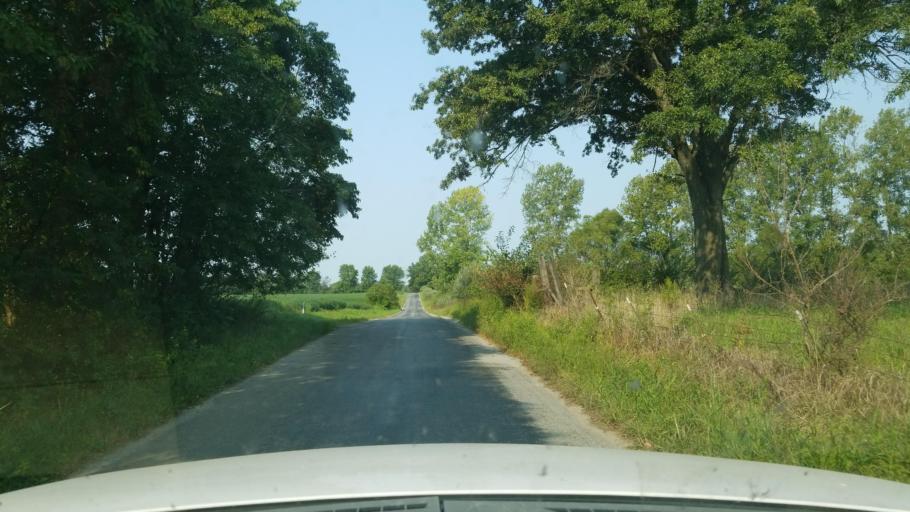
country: US
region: Illinois
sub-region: Saline County
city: Carrier Mills
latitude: 37.7906
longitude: -88.6651
